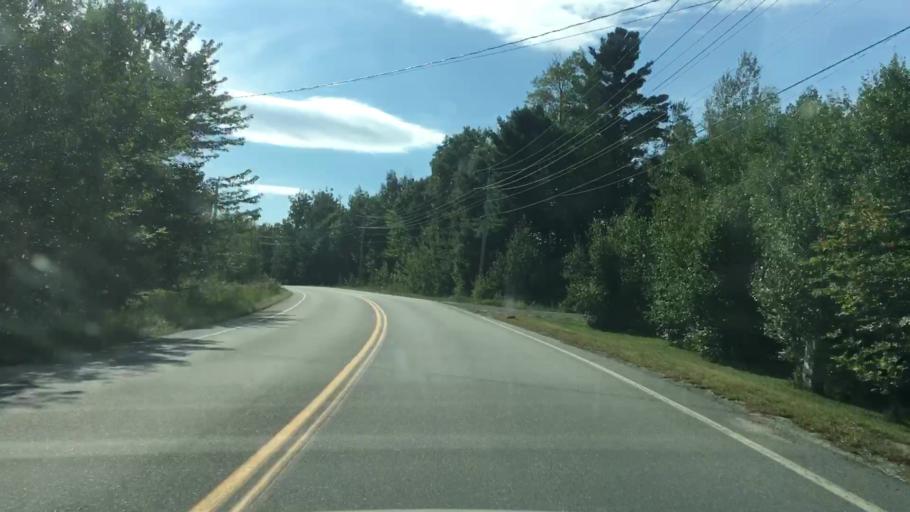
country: US
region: Maine
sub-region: Penobscot County
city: Lincoln
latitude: 45.3934
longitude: -68.5275
